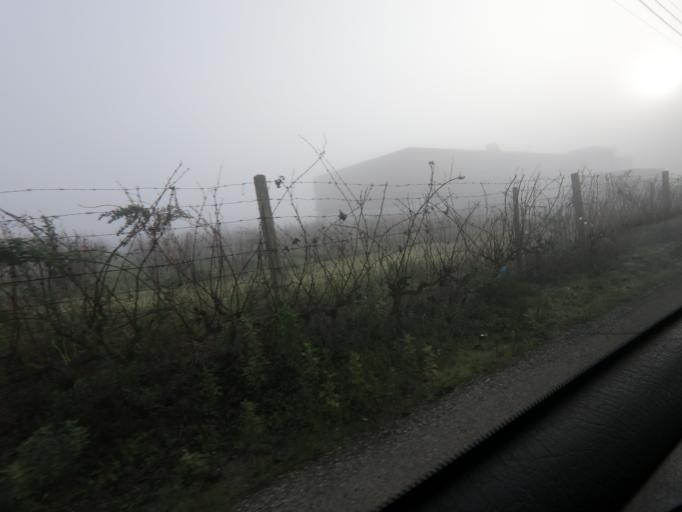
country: PT
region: Setubal
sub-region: Palmela
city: Palmela
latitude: 38.5947
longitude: -8.8419
